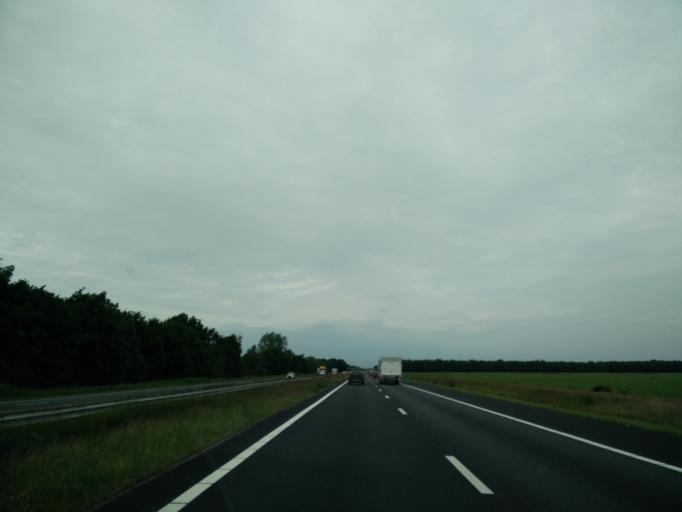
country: NL
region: Drenthe
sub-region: Gemeente Assen
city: Assen
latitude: 52.9374
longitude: 6.5378
